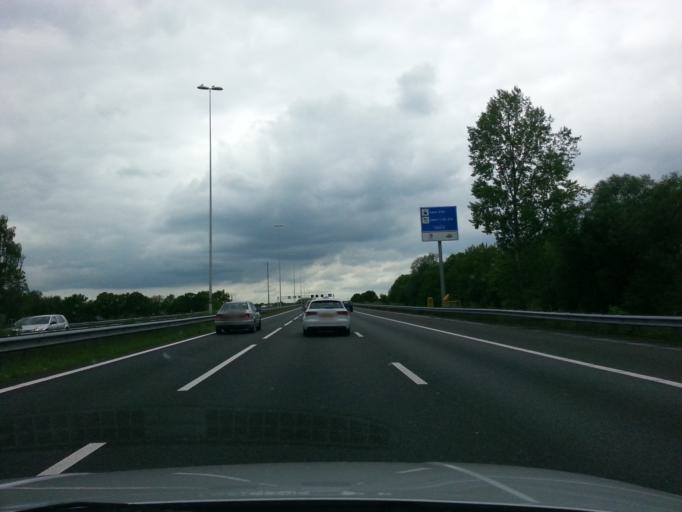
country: NL
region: Utrecht
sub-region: Gemeente Utrechtse Heuvelrug
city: Overberg
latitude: 52.0477
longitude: 5.4963
